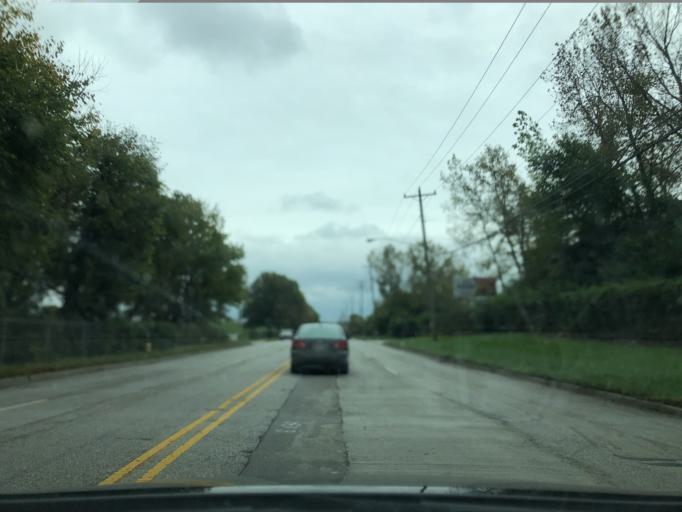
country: US
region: Kentucky
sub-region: Campbell County
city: Fort Thomas
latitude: 39.1065
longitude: -84.4356
